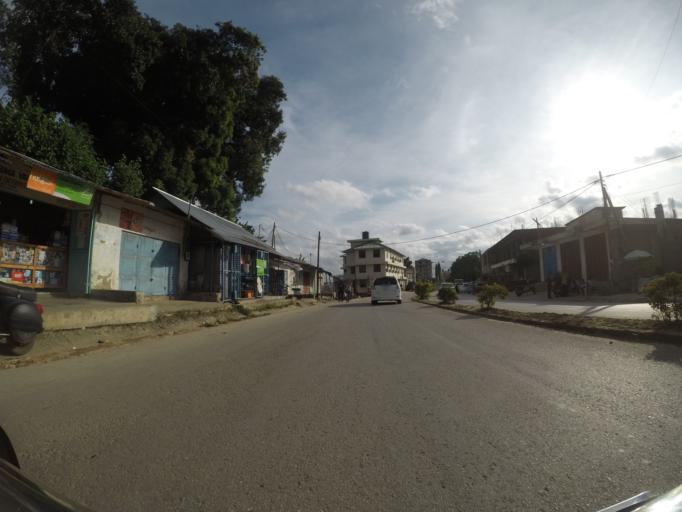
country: TZ
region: Pemba South
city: Chake Chake
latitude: -5.2403
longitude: 39.7694
